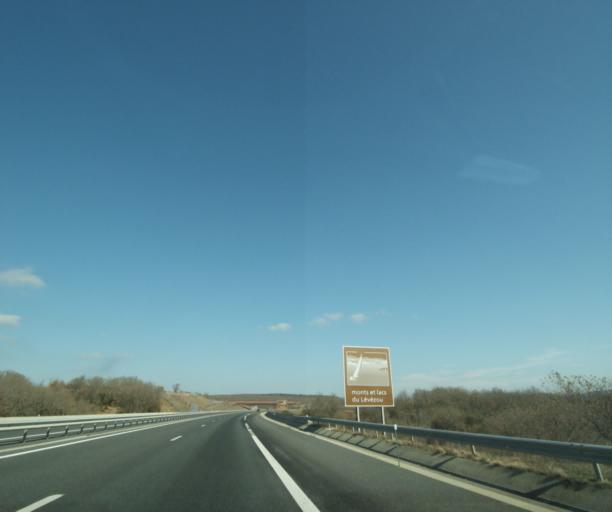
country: FR
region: Midi-Pyrenees
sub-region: Departement de l'Aveyron
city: Creissels
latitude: 44.1495
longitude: 3.0174
